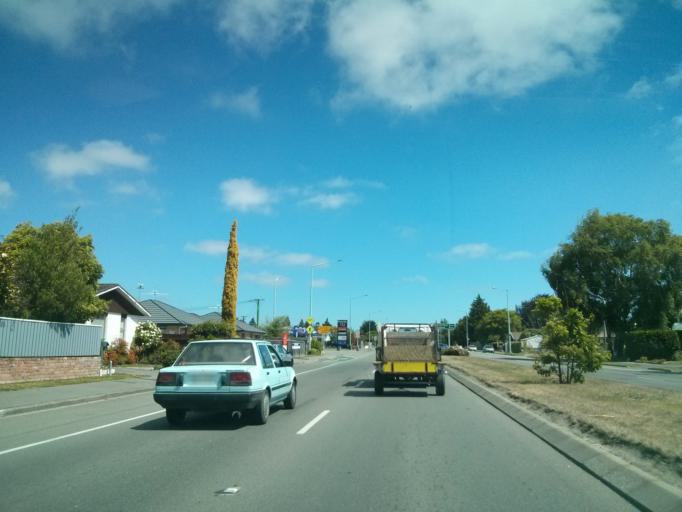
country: NZ
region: Canterbury
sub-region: Waimakariri District
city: Kaiapoi
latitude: -43.4482
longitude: 172.6303
